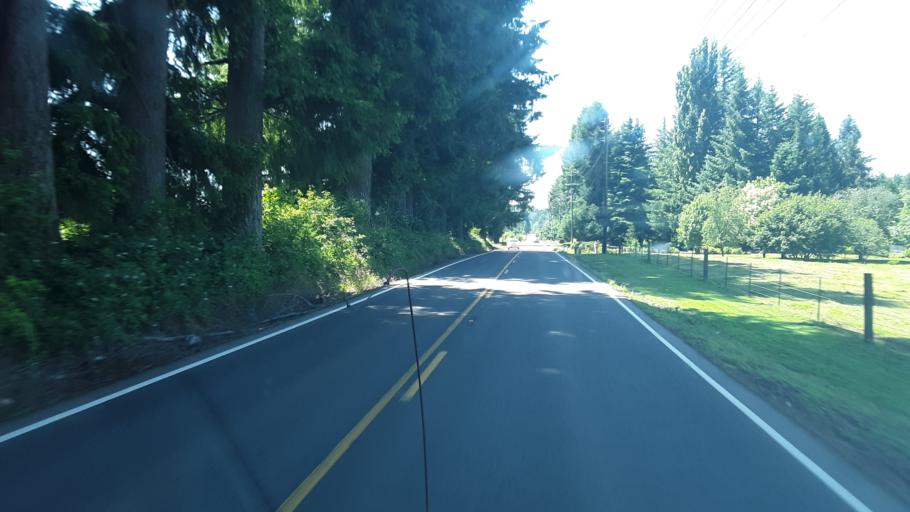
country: US
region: Washington
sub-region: Clark County
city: Amboy
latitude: 45.9243
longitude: -122.4032
